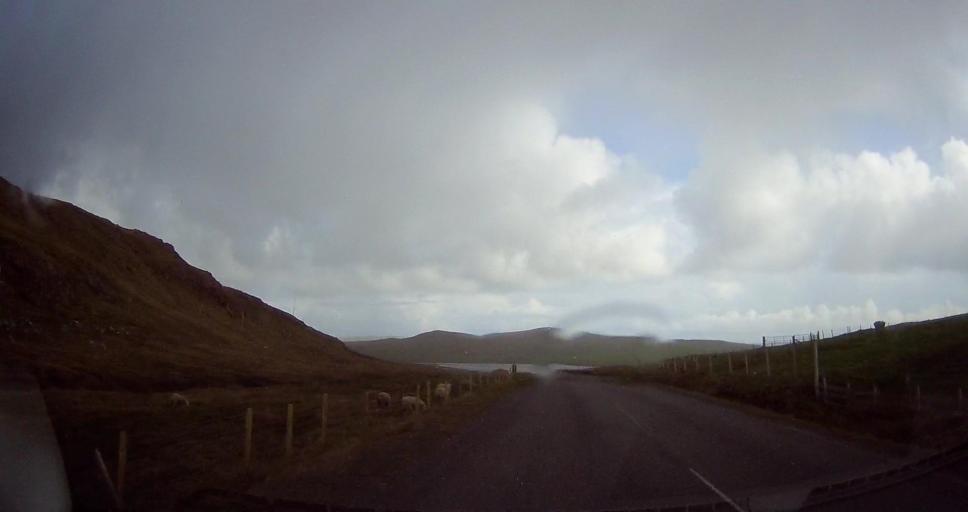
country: GB
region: Scotland
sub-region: Shetland Islands
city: Lerwick
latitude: 60.5433
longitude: -1.3438
